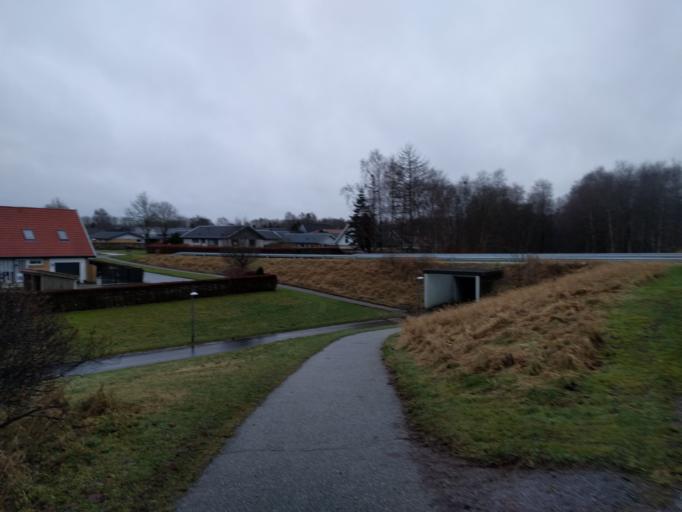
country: DK
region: Central Jutland
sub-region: Viborg Kommune
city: Viborg
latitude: 56.4302
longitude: 9.3947
